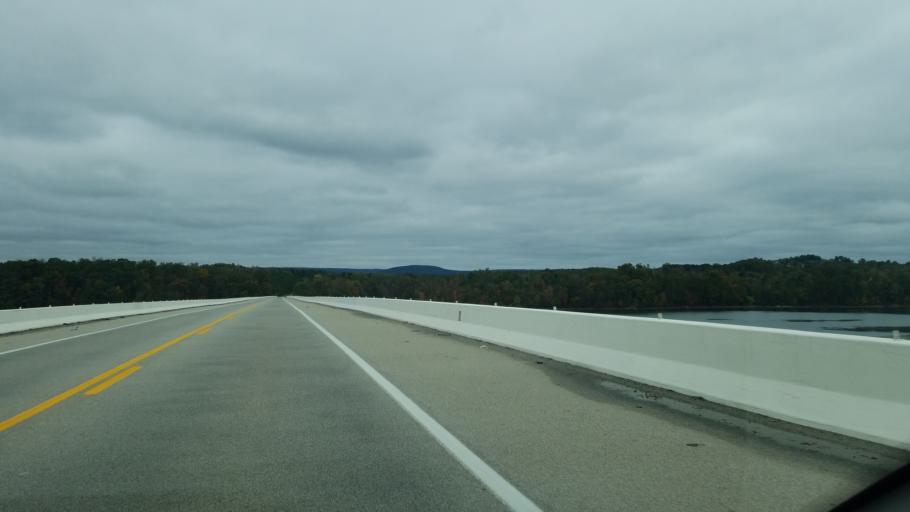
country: US
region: Tennessee
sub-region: Rhea County
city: Graysville
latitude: 35.4088
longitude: -85.0183
